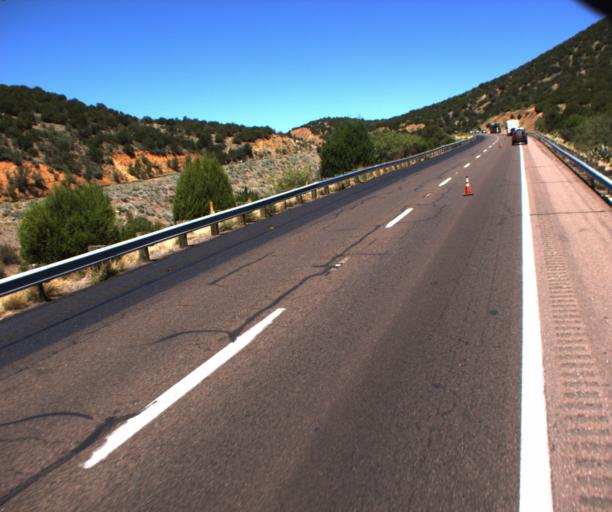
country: US
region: Arizona
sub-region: Gila County
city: Payson
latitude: 34.1605
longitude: -111.3220
